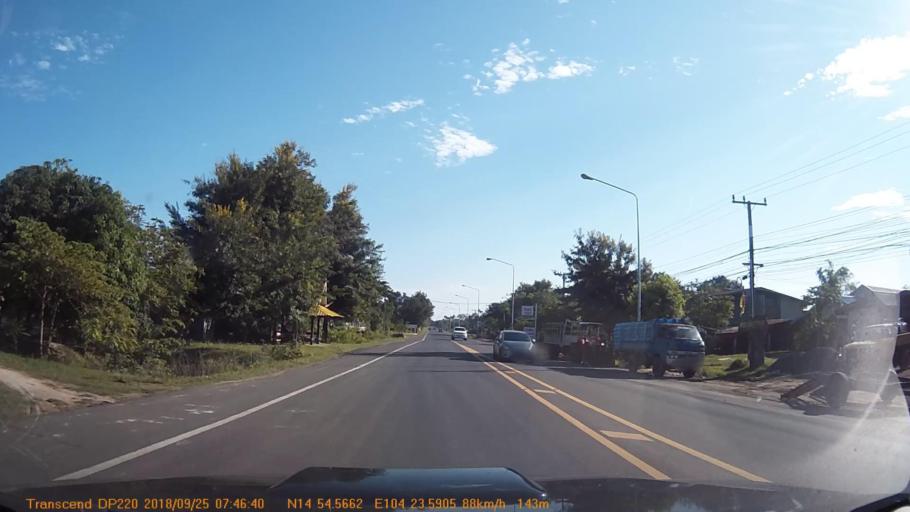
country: TH
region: Sisaket
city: Phayu
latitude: 14.9097
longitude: 104.3933
